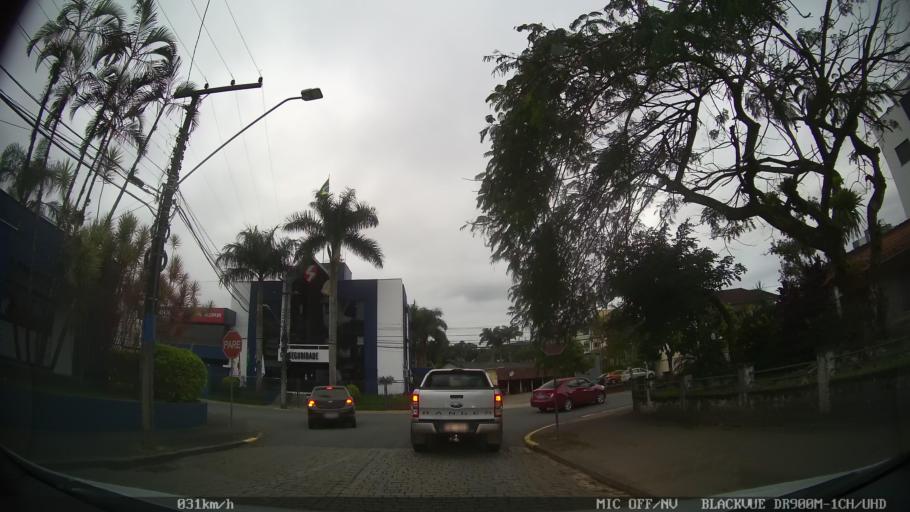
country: BR
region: Santa Catarina
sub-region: Joinville
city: Joinville
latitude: -26.2843
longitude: -48.8453
